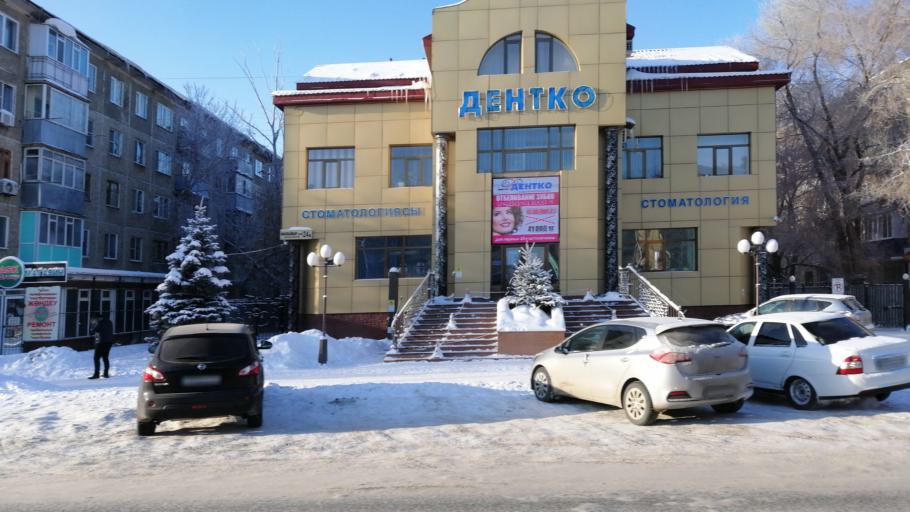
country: KZ
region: Aqtoebe
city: Aqtobe
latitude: 50.3049
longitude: 57.1513
